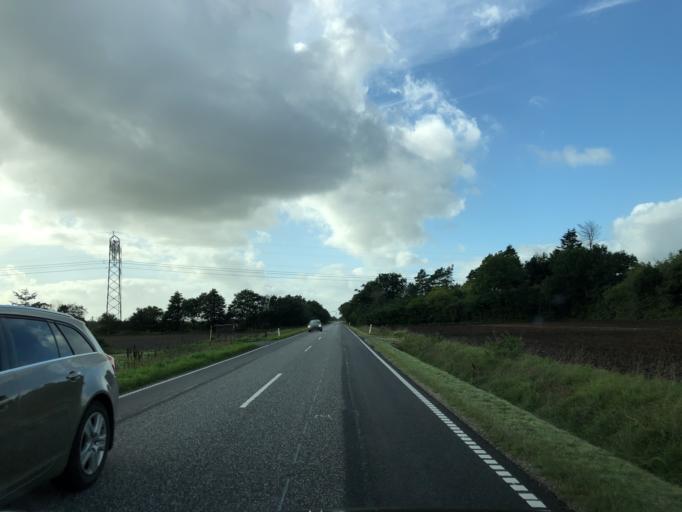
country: DK
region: Central Jutland
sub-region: Holstebro Kommune
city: Holstebro
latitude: 56.3704
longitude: 8.5495
